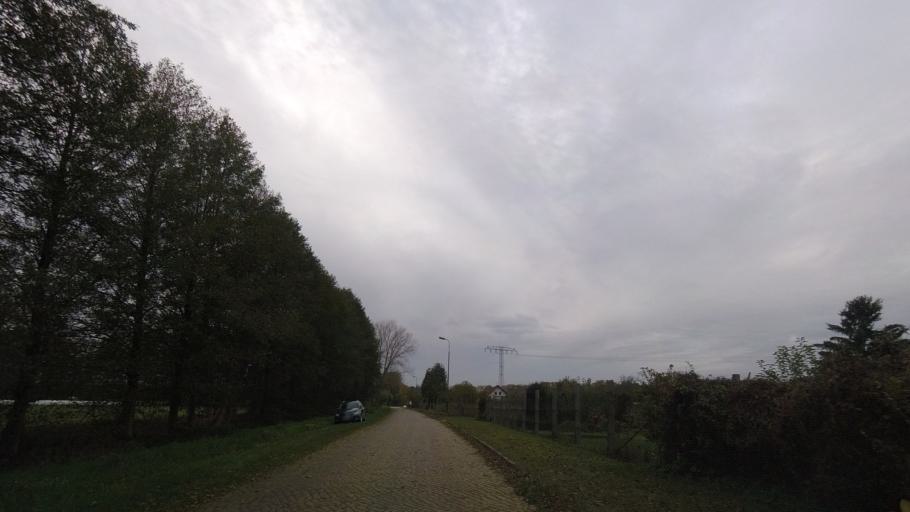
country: DE
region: Brandenburg
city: Treuenbrietzen
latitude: 52.0935
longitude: 12.8811
